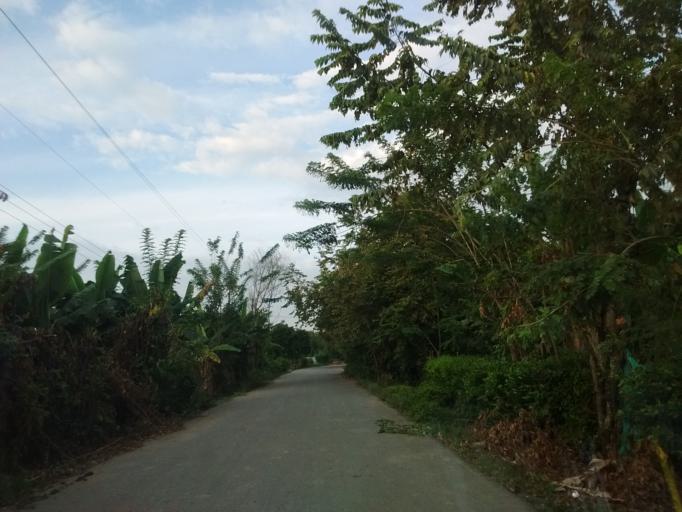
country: CO
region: Cauca
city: Puerto Tejada
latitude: 3.2203
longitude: -76.4485
